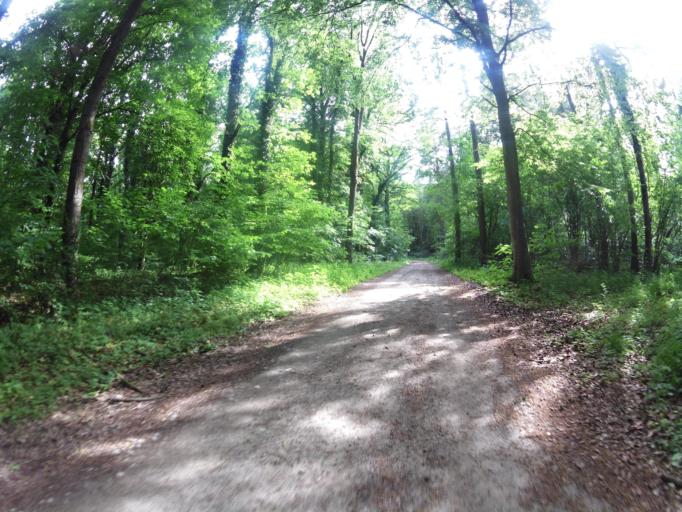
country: DE
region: Bavaria
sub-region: Regierungsbezirk Unterfranken
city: Ochsenfurt
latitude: 49.6871
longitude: 10.0712
